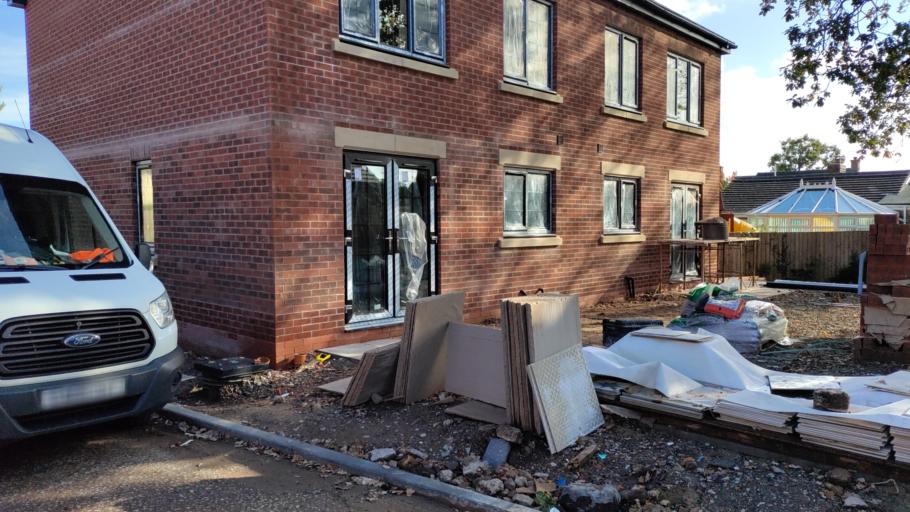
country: GB
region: England
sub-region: Cheshire West and Chester
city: Hartford
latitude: 53.2438
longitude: -2.5472
